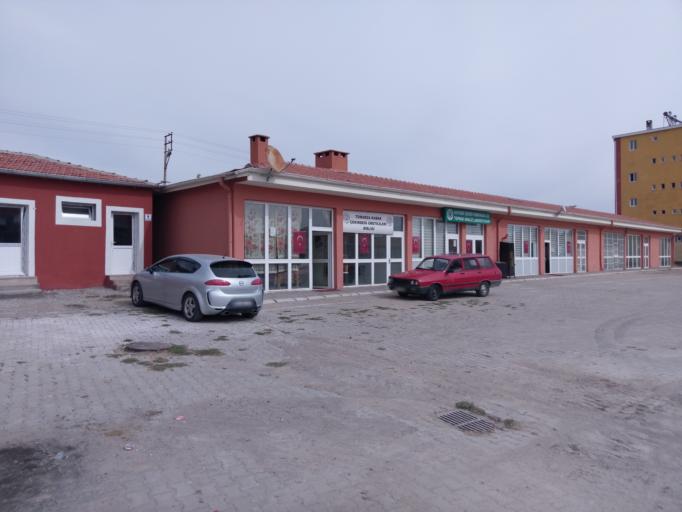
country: TR
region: Kayseri
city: Tomarza
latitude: 38.4475
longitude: 35.8038
